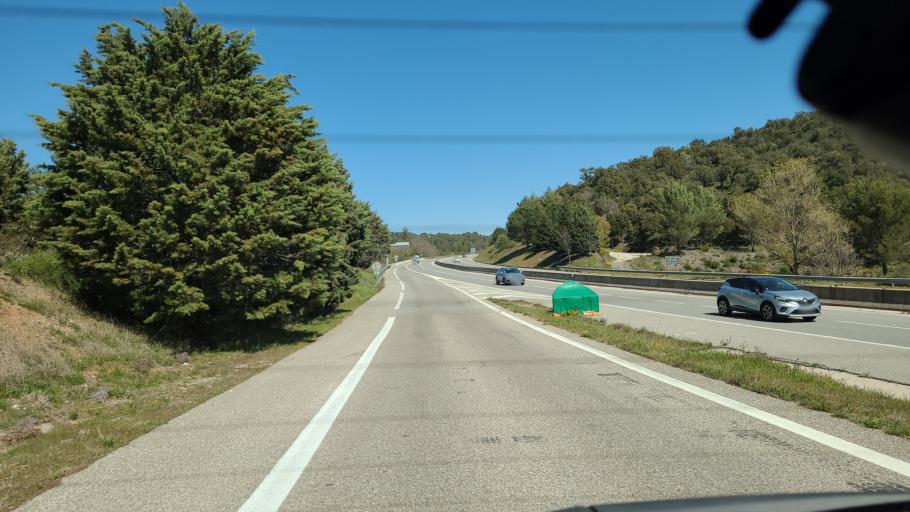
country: FR
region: Provence-Alpes-Cote d'Azur
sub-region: Departement du Var
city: Carnoules
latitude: 43.2851
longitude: 6.1889
